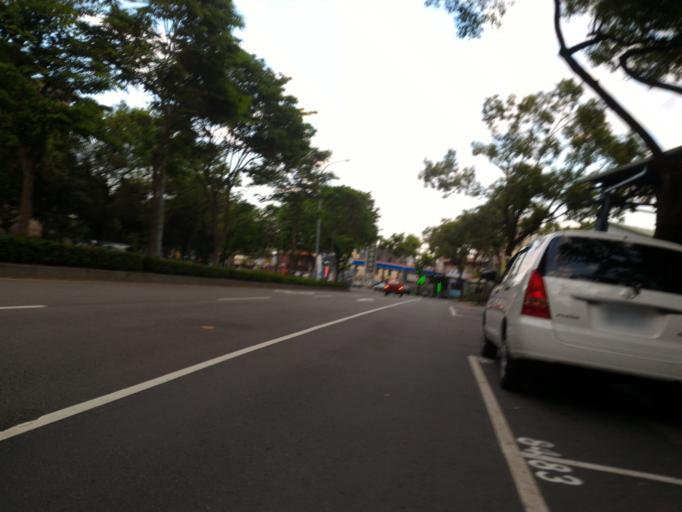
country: TW
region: Taiwan
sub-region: Taoyuan
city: Taoyuan
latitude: 24.9452
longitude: 121.3845
